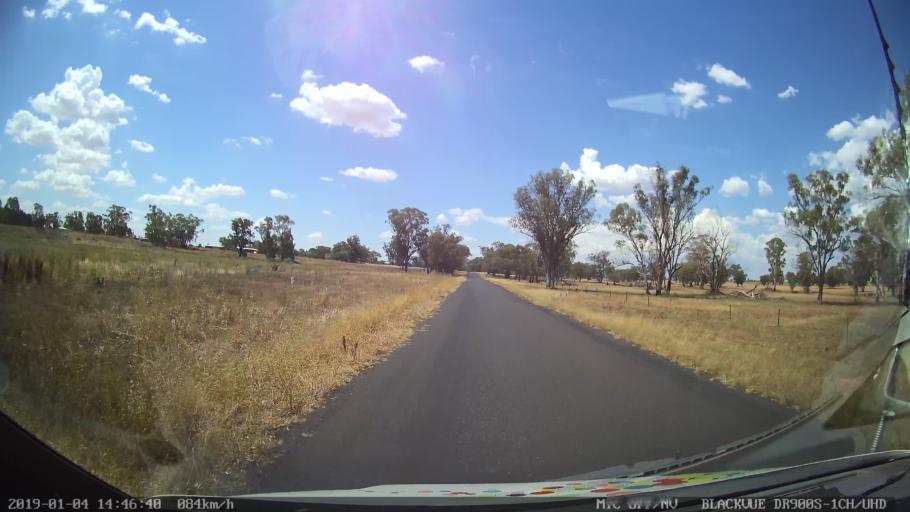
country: AU
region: New South Wales
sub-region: Dubbo Municipality
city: Dubbo
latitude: -32.0786
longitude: 148.6587
